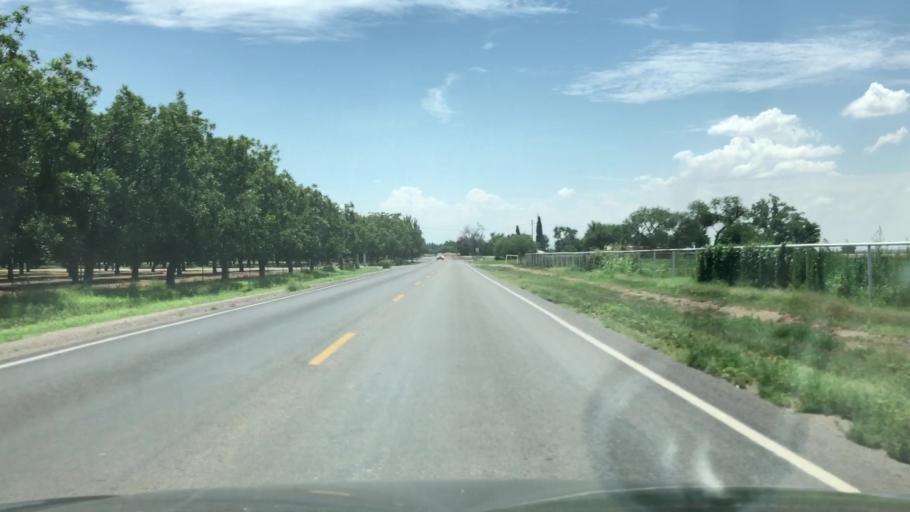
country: US
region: New Mexico
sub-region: Dona Ana County
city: Anthony
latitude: 32.0126
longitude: -106.6663
